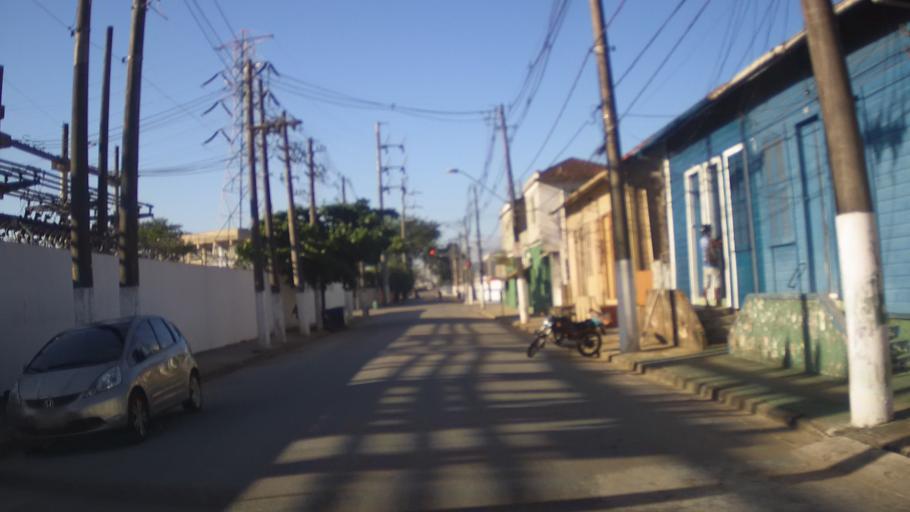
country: BR
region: Sao Paulo
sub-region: Santos
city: Santos
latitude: -23.9413
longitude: -46.3397
